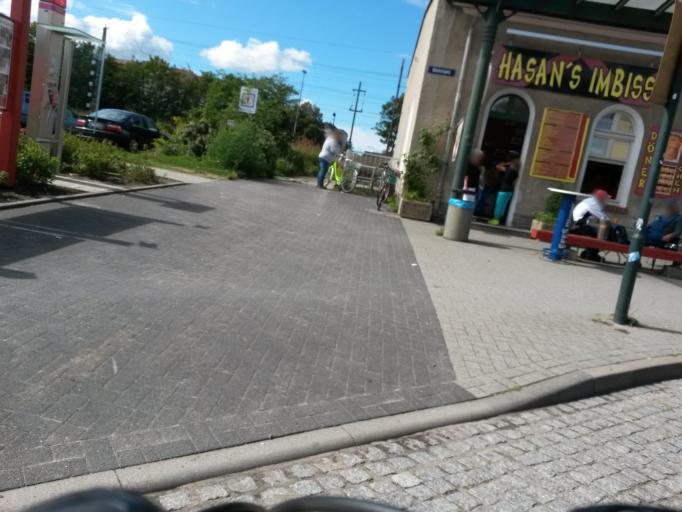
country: DE
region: Brandenburg
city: Angermunde
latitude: 53.0150
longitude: 13.9975
